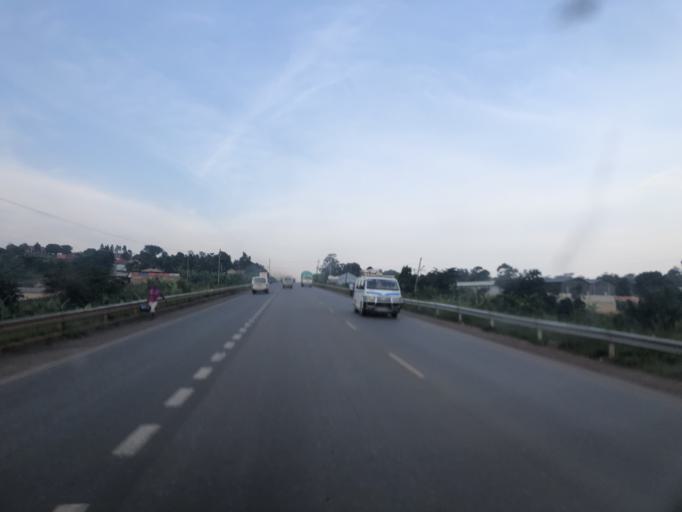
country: UG
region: Central Region
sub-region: Mpigi District
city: Mpigi
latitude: 0.2434
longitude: 32.3719
